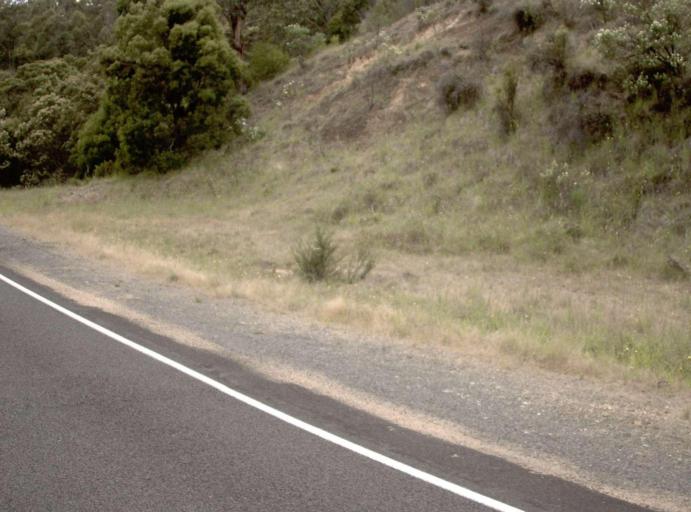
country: AU
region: New South Wales
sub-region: Bombala
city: Bombala
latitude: -37.2437
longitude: 149.2592
